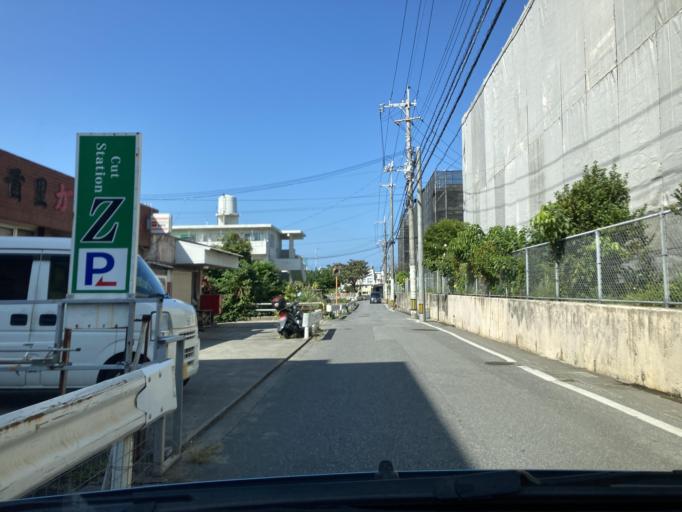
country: JP
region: Okinawa
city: Naha-shi
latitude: 26.2256
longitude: 127.7252
